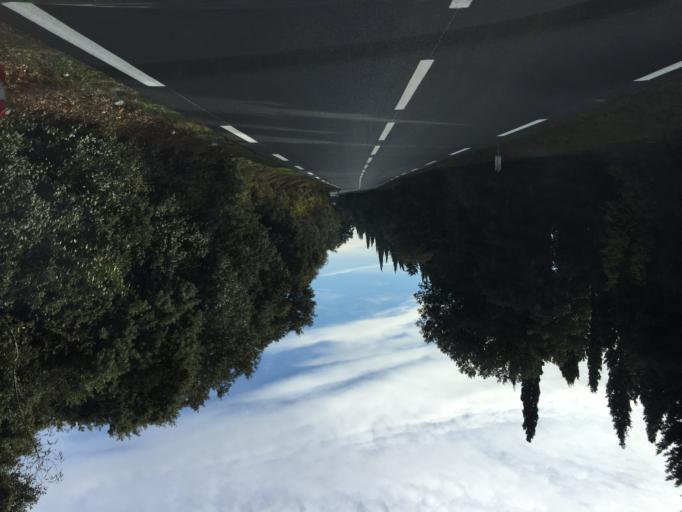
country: FR
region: Provence-Alpes-Cote d'Azur
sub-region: Departement du Vaucluse
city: Serignan-du-Comtat
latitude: 44.1731
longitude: 4.8149
